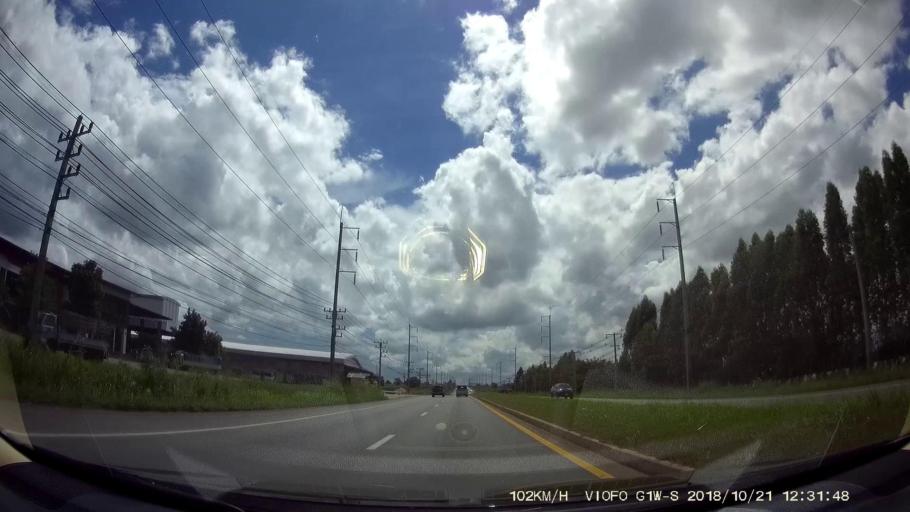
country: TH
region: Nakhon Ratchasima
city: Dan Khun Thot
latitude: 15.1511
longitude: 101.7333
